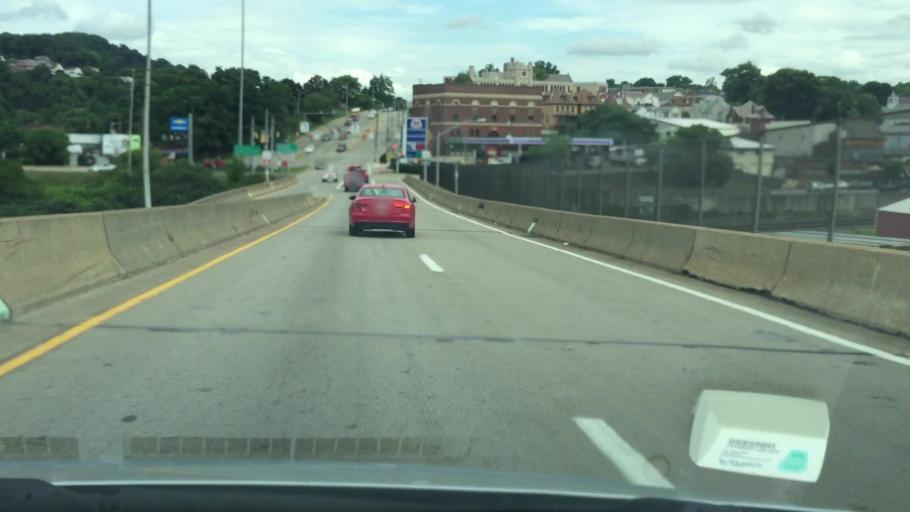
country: US
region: Pennsylvania
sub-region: Allegheny County
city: Tarentum
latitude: 40.6001
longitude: -79.7568
